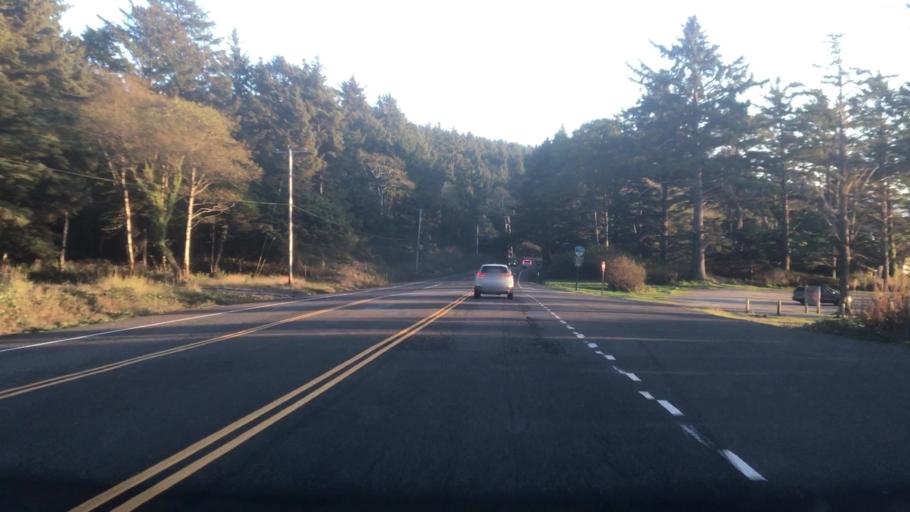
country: US
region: Oregon
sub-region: Clatsop County
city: Cannon Beach
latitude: 45.8471
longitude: -123.9602
